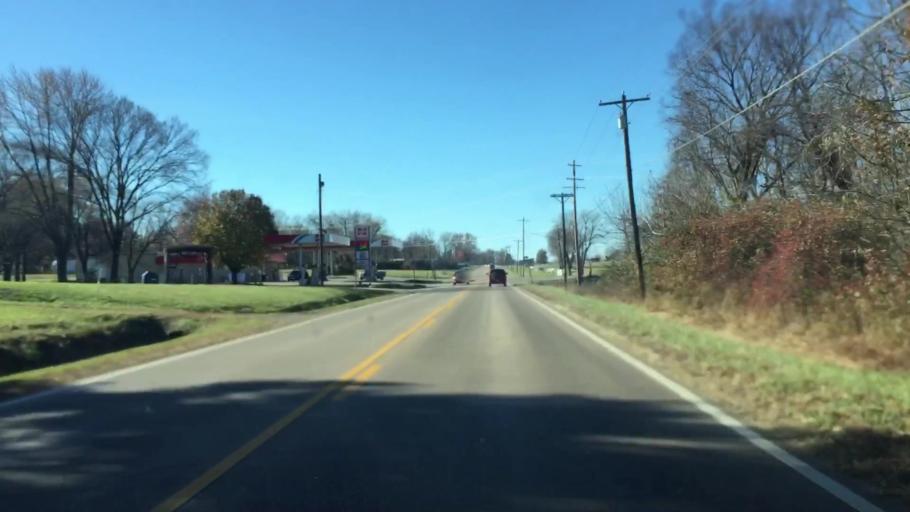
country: US
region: Missouri
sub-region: Miller County
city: Eldon
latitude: 38.3576
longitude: -92.5651
